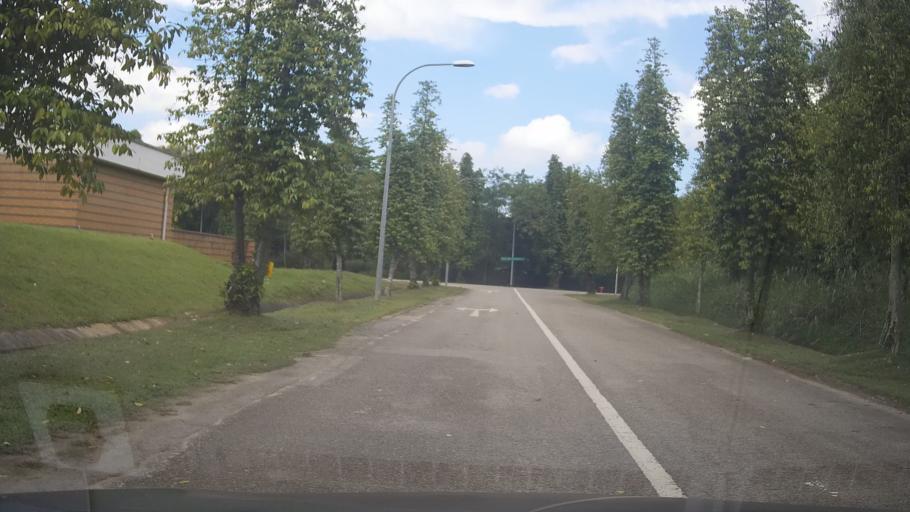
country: MY
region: Johor
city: Kampung Pasir Gudang Baru
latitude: 1.3859
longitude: 103.9350
